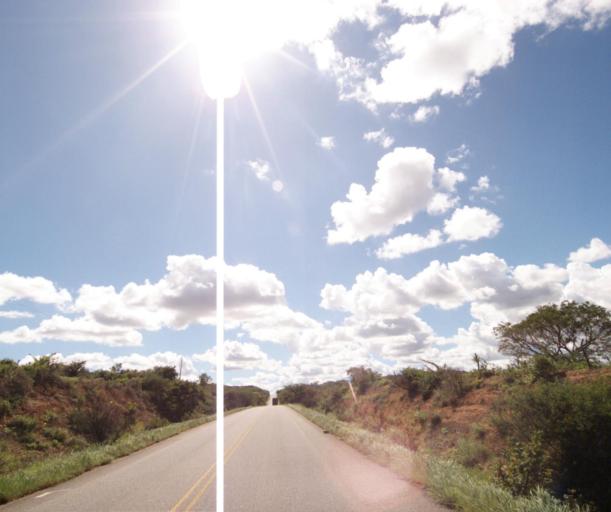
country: BR
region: Bahia
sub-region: Caetite
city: Caetite
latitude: -14.1718
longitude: -42.2039
